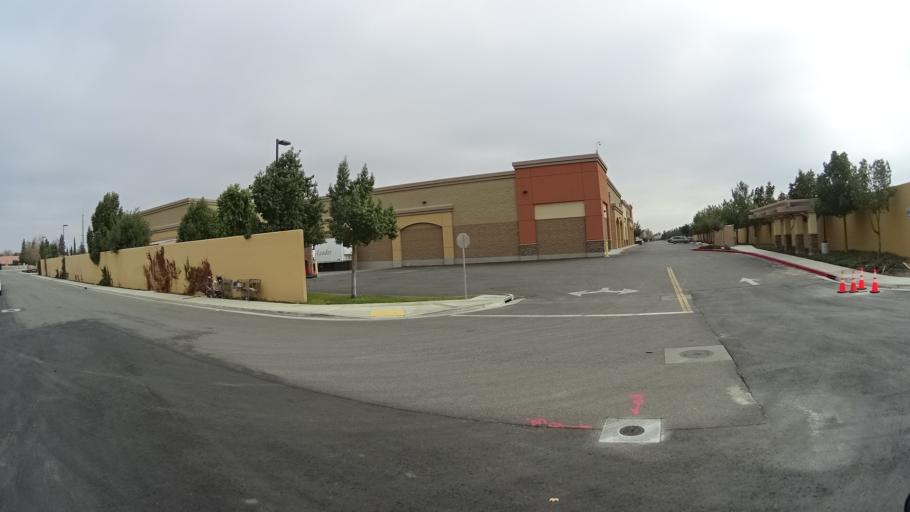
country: US
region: California
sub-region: Kern County
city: Greenfield
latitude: 35.2944
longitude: -119.0790
